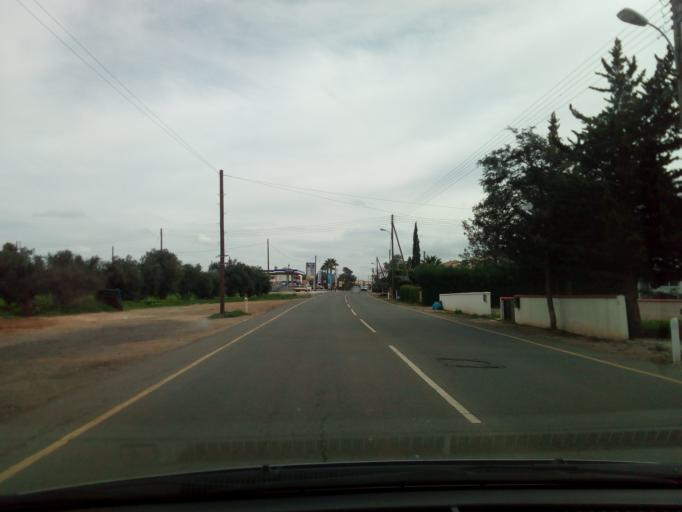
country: CY
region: Lefkosia
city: Astromeritis
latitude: 35.1385
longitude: 33.0519
